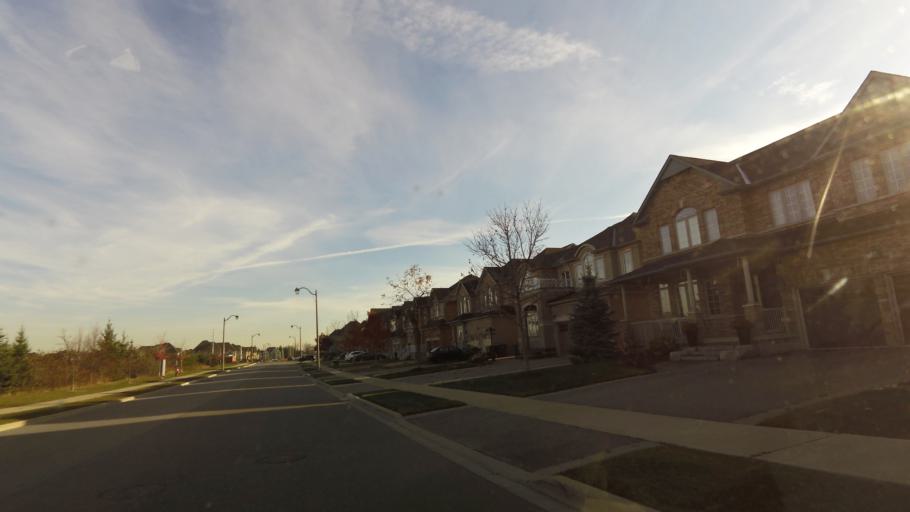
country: CA
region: Ontario
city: Brampton
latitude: 43.7893
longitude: -79.7459
